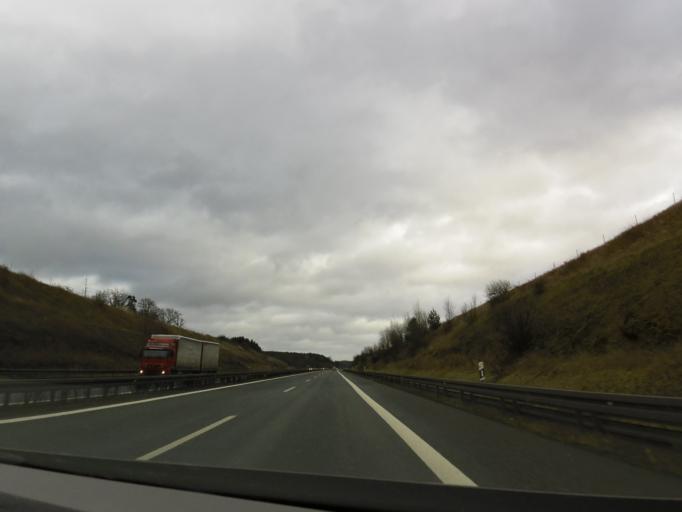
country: DE
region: Bavaria
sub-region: Upper Franconia
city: Gattendorf
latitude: 50.3449
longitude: 11.9933
